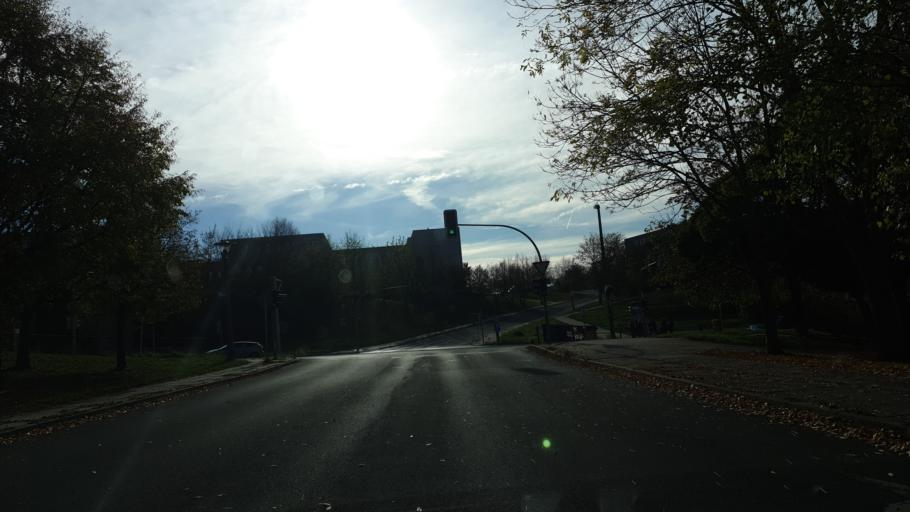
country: DE
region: Thuringia
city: Gera
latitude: 50.9027
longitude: 12.0929
